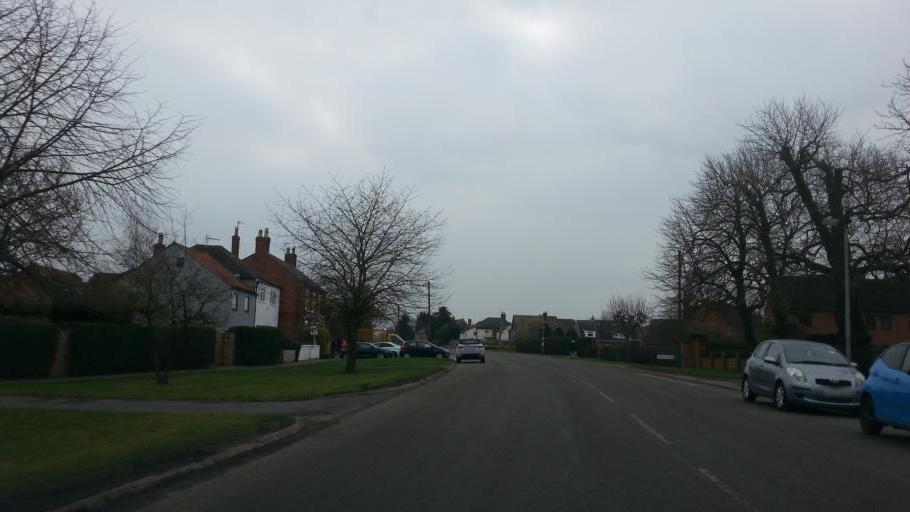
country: GB
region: England
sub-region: Lincolnshire
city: Long Bennington
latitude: 52.9937
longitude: -0.7586
